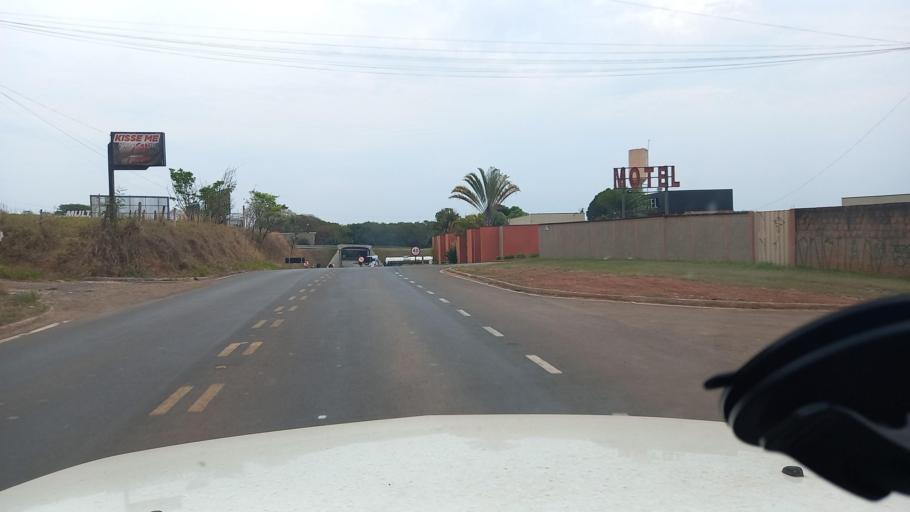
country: BR
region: Sao Paulo
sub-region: Moji-Guacu
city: Mogi-Gaucu
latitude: -22.3740
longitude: -46.9688
